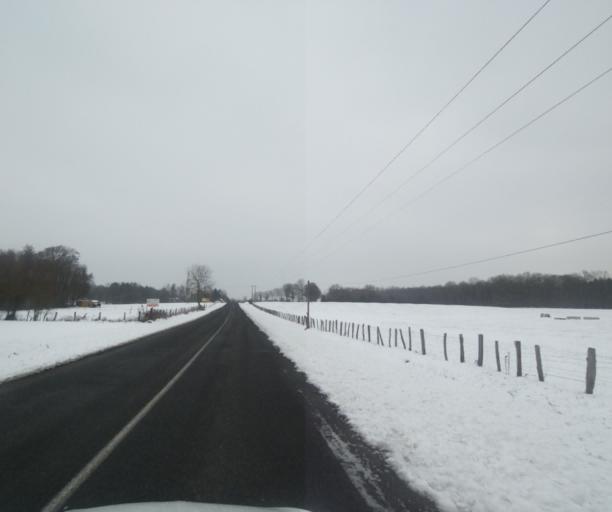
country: FR
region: Champagne-Ardenne
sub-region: Departement de la Haute-Marne
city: Villiers-en-Lieu
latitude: 48.6122
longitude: 4.8870
